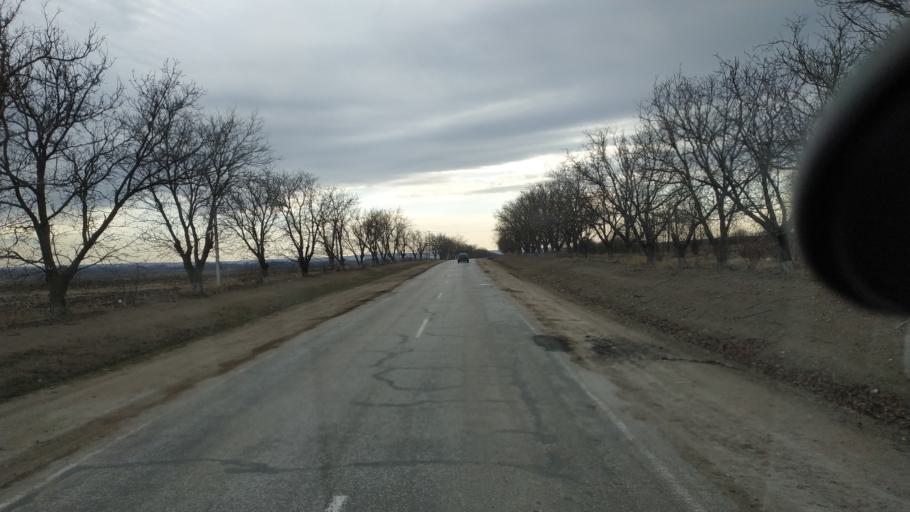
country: MD
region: Criuleni
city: Criuleni
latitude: 47.1970
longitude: 29.1511
